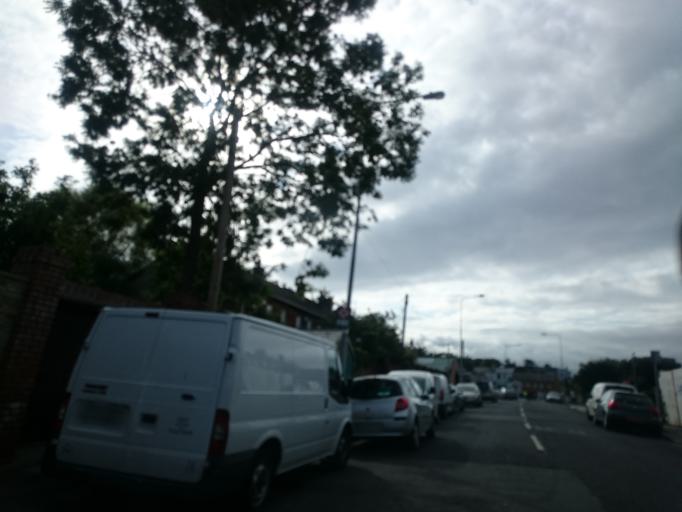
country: IE
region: Leinster
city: Rathgar
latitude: 53.3175
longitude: -6.2776
